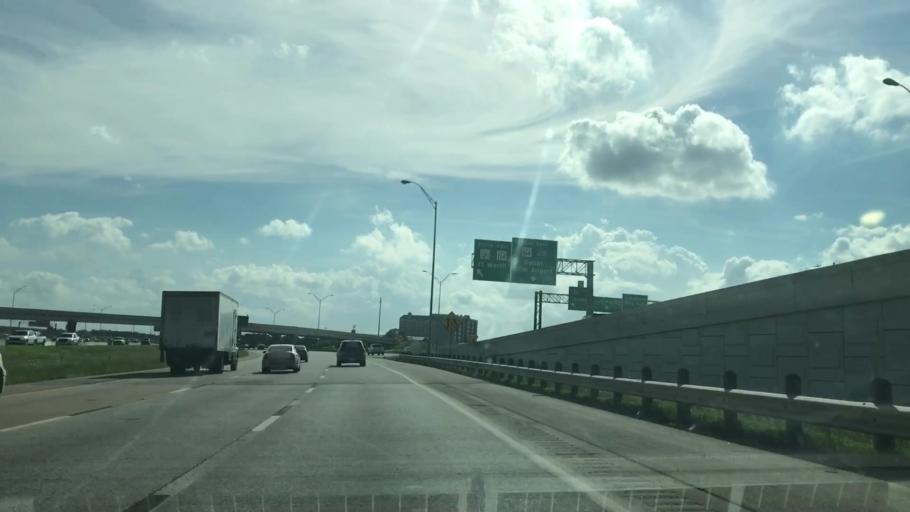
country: US
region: Texas
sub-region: Dallas County
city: Coppell
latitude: 32.9636
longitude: -97.0381
